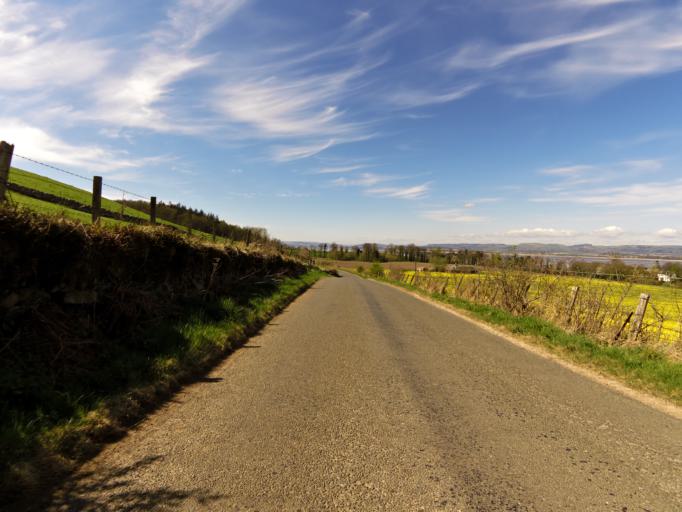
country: GB
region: Scotland
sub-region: Perth and Kinross
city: Errol
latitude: 56.3875
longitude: -3.1079
